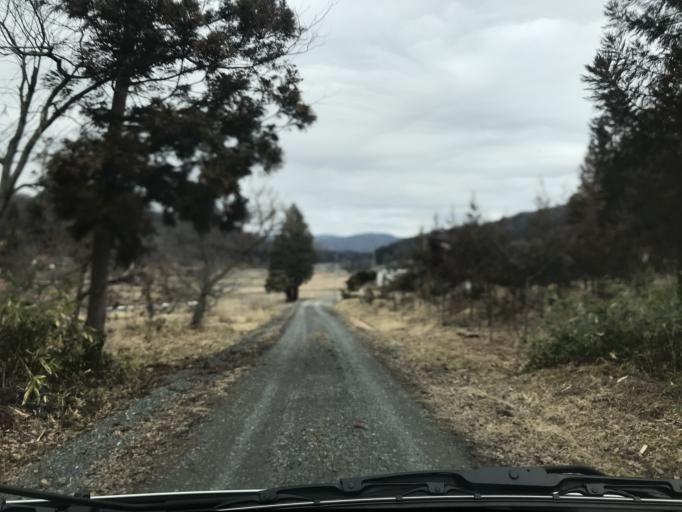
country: JP
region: Iwate
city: Kitakami
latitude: 39.3216
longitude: 141.2278
